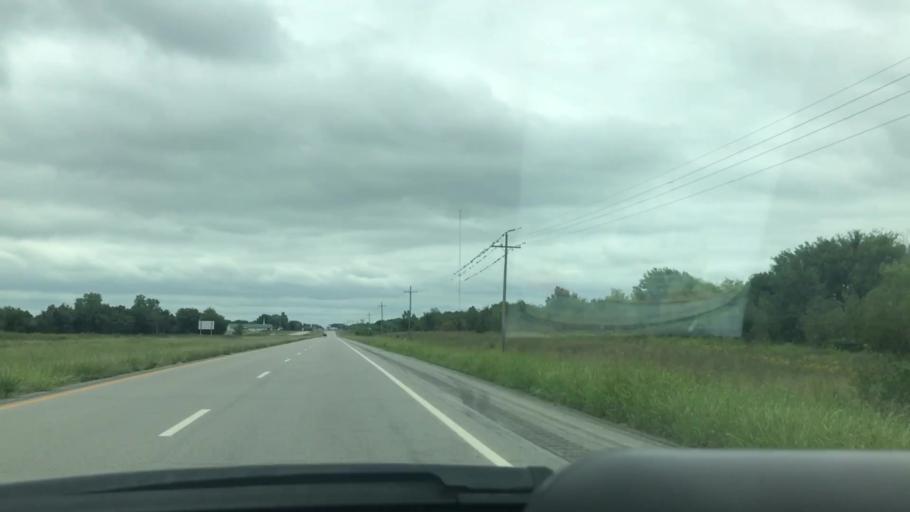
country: US
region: Oklahoma
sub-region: Mayes County
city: Pryor
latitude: 36.4167
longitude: -95.2790
